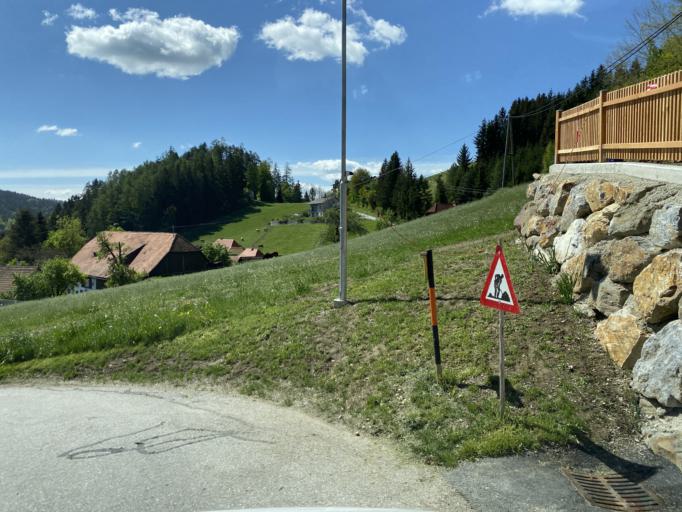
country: AT
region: Styria
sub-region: Politischer Bezirk Weiz
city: Koglhof
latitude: 47.3201
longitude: 15.6890
